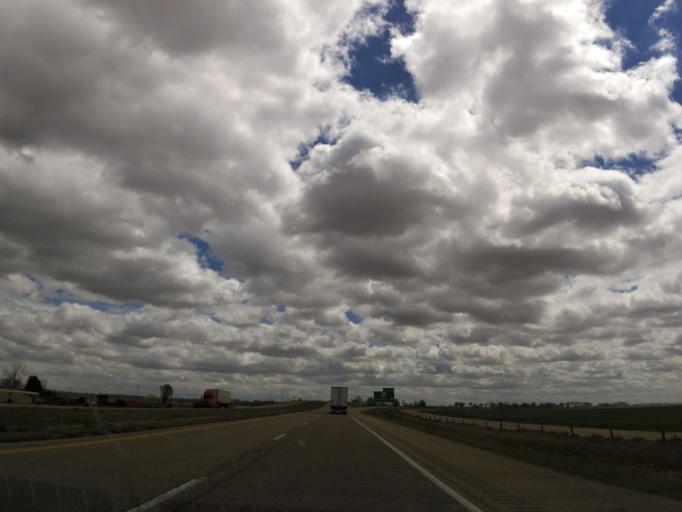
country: US
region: Arkansas
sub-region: Poinsett County
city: Trumann
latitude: 35.6349
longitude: -90.5049
